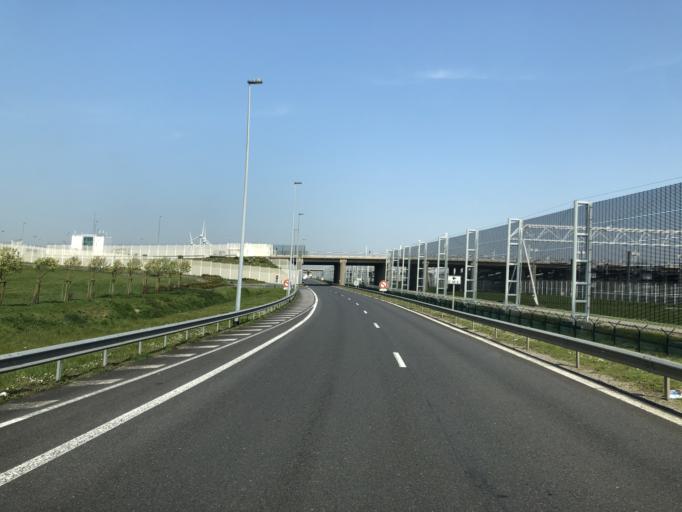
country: FR
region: Nord-Pas-de-Calais
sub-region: Departement du Pas-de-Calais
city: Frethun
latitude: 50.9209
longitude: 1.8100
